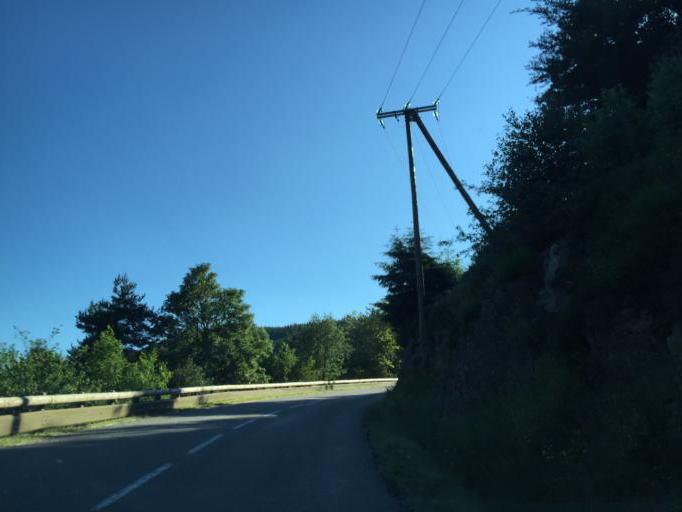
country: FR
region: Rhone-Alpes
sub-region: Departement de la Loire
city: Saint-Chamond
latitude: 45.3891
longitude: 4.5342
